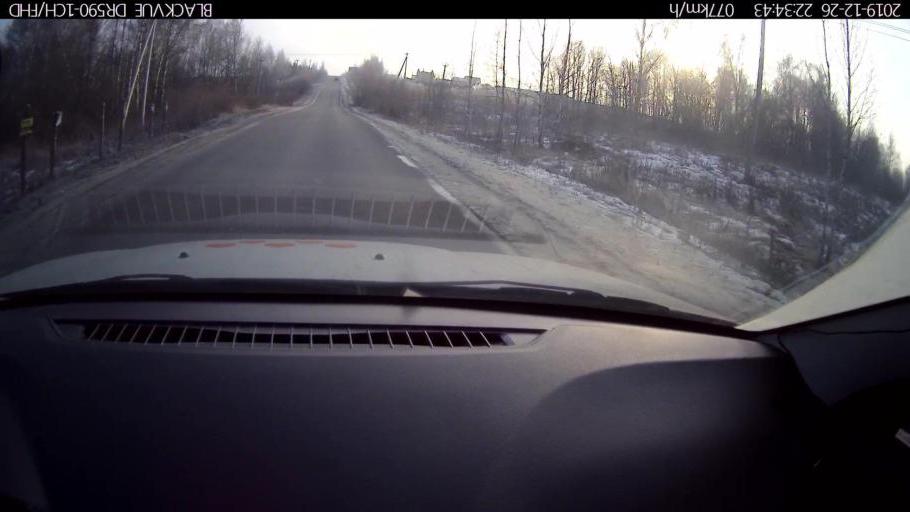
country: RU
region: Nizjnij Novgorod
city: Burevestnik
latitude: 56.1538
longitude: 43.7124
